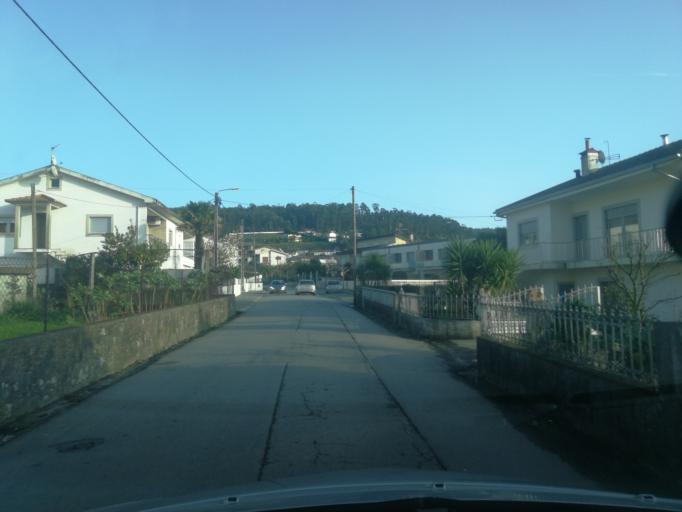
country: PT
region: Braga
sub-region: Barcelos
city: Galegos
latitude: 41.5171
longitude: -8.5658
